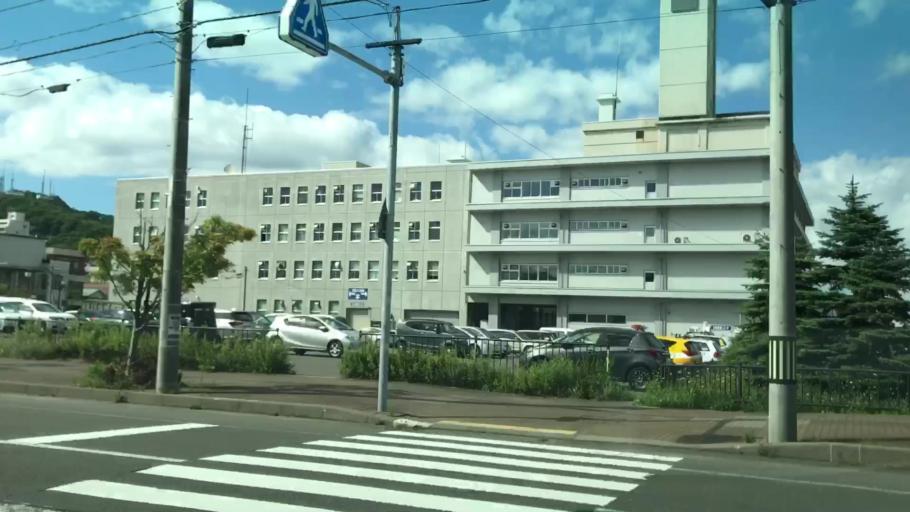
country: JP
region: Hokkaido
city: Muroran
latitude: 42.3144
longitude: 140.9744
